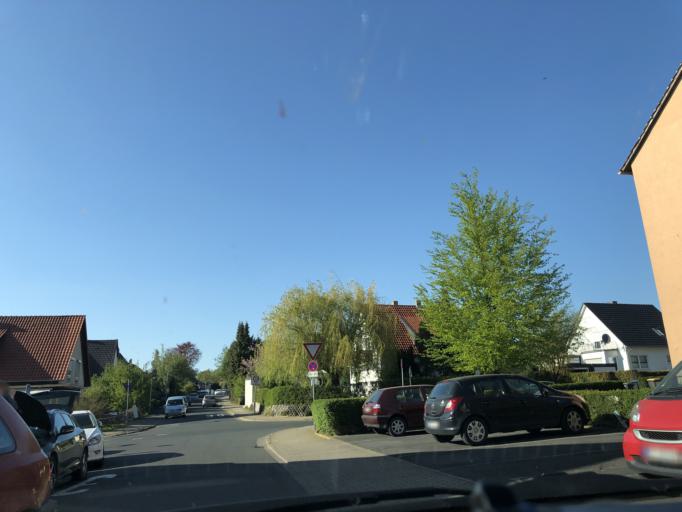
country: DE
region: Lower Saxony
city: Wolfenbuettel
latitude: 52.1703
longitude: 10.5617
